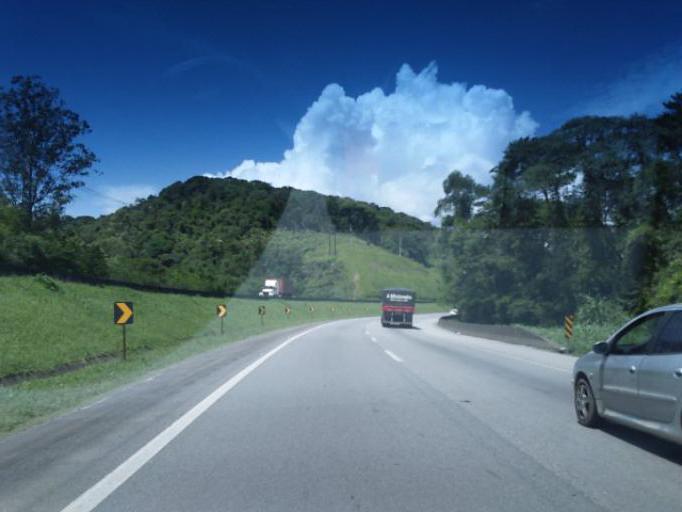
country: BR
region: Sao Paulo
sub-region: Juquitiba
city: Juquitiba
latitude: -23.9397
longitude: -47.0412
